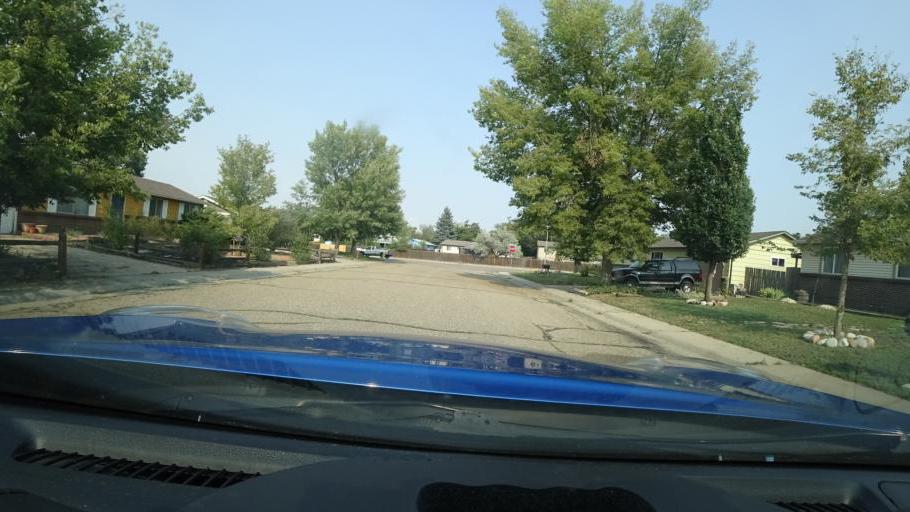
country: US
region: Colorado
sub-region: Adams County
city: Aurora
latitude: 39.6662
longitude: -104.8031
